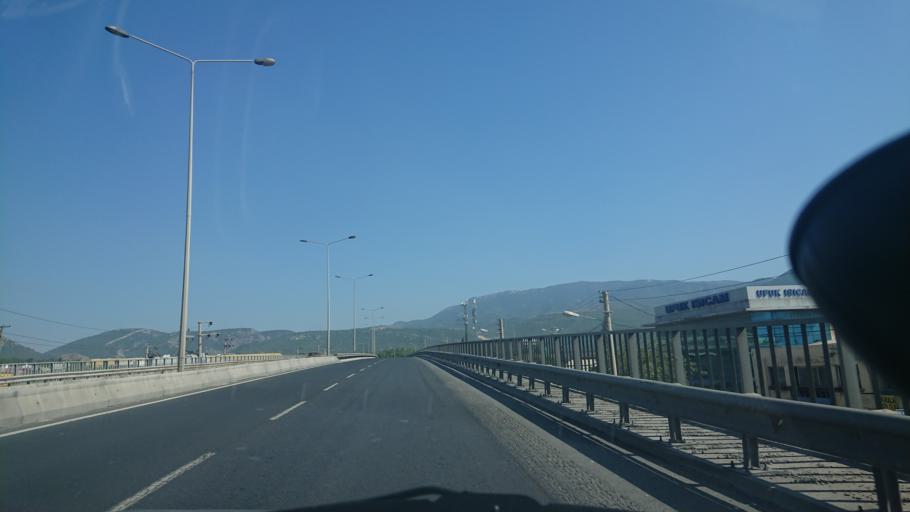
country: TR
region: Izmir
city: Bornova
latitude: 38.4530
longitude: 27.2641
